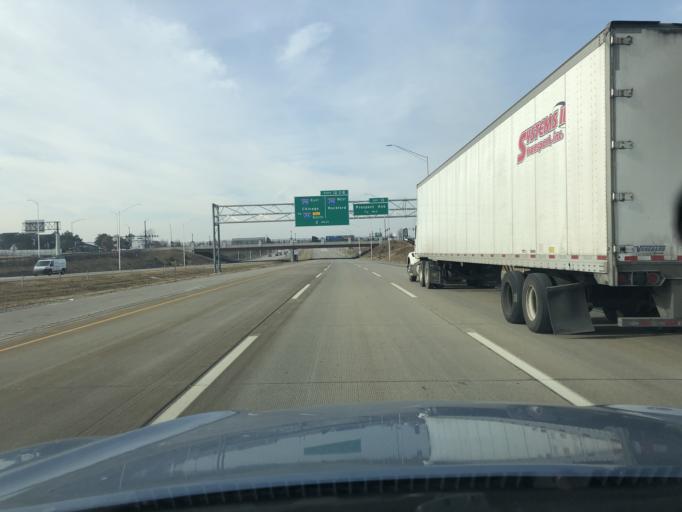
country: US
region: Illinois
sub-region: DuPage County
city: Wood Dale
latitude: 41.9838
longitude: -87.9769
